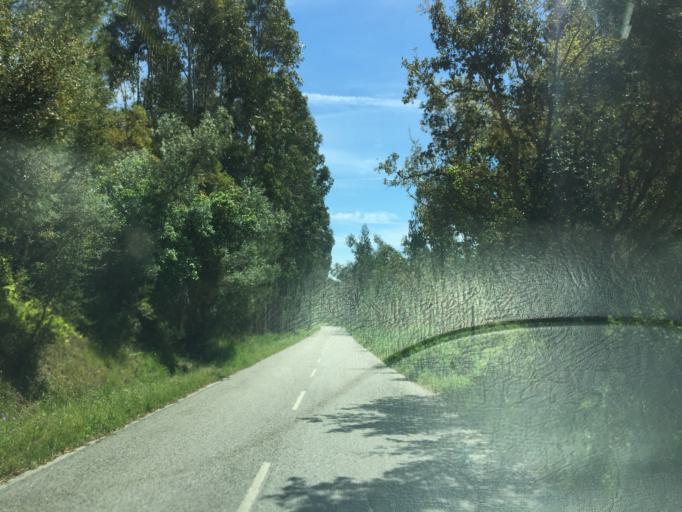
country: PT
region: Coimbra
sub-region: Figueira da Foz
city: Lavos
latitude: 40.0693
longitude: -8.7642
